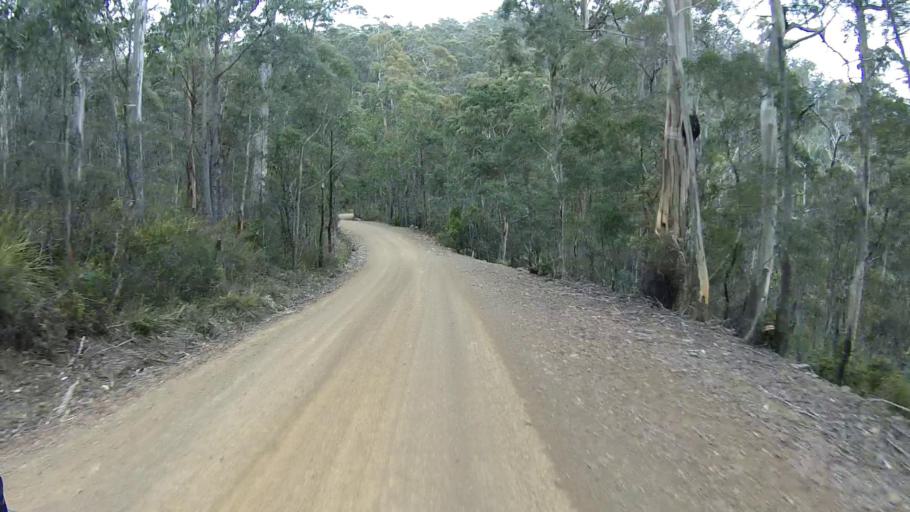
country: AU
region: Tasmania
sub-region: Sorell
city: Sorell
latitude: -42.6075
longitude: 147.8783
